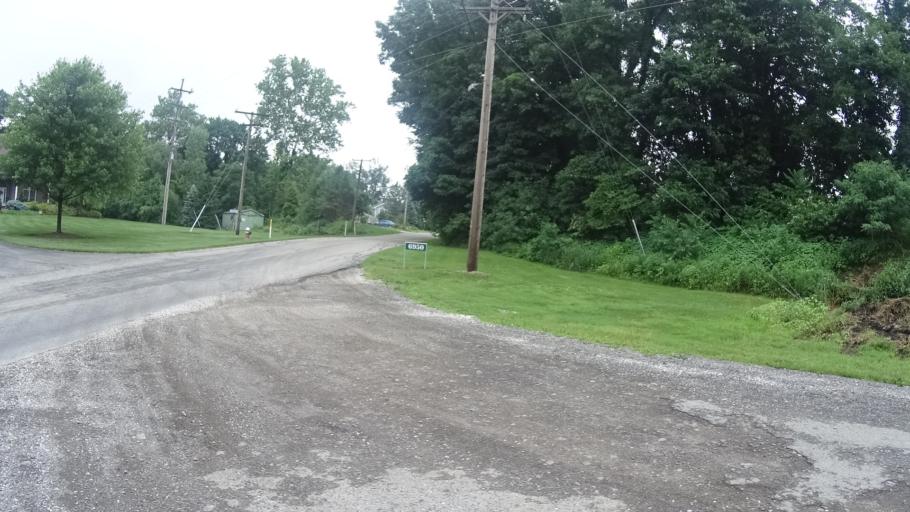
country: US
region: Ohio
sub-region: Erie County
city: Huron
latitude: 41.3155
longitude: -82.4954
